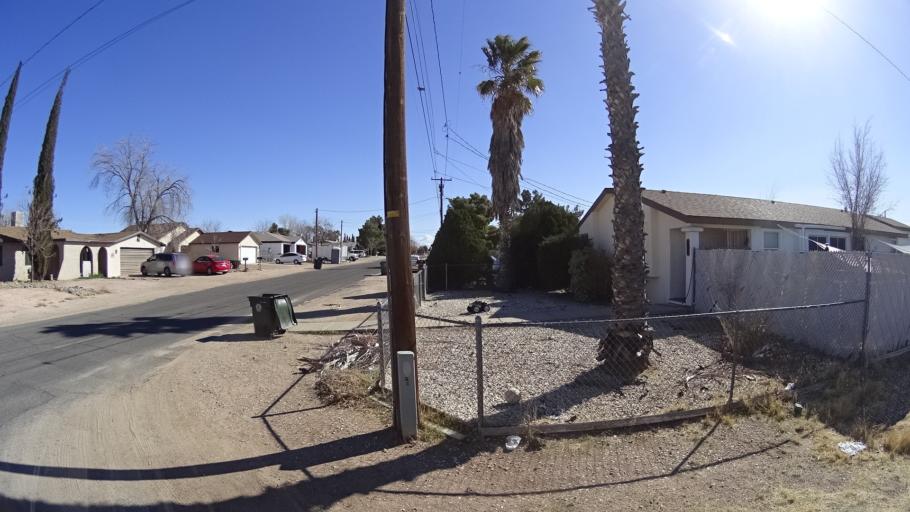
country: US
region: Arizona
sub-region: Mohave County
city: Kingman
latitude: 35.1971
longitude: -114.0223
